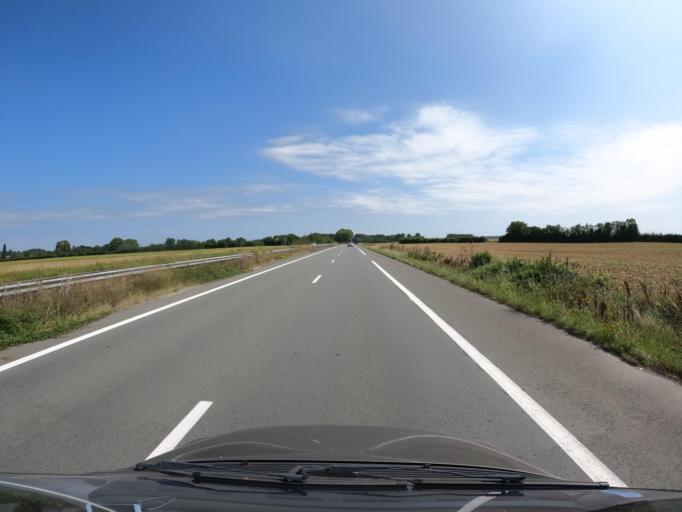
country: FR
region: Poitou-Charentes
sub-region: Departement des Deux-Sevres
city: Mauze-sur-le-Mignon
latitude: 46.2024
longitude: -0.6499
